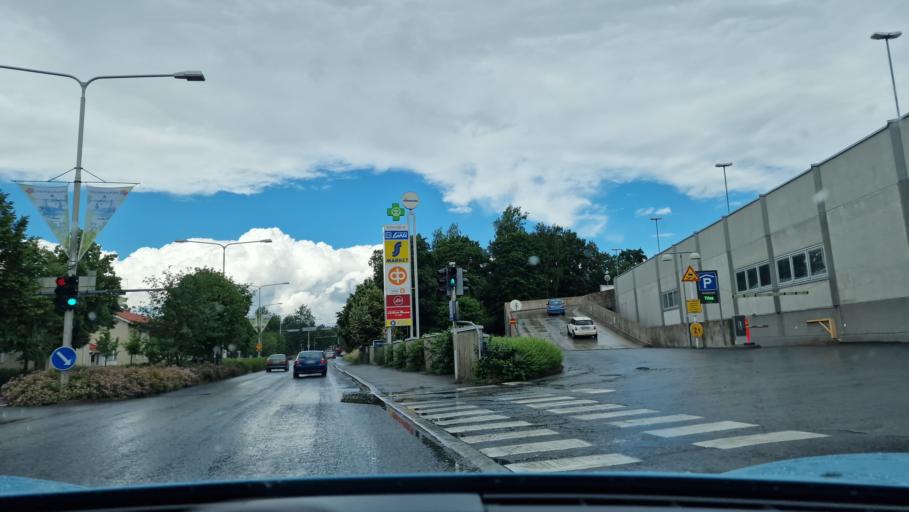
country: FI
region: Pirkanmaa
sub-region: Etelae-Pirkanmaa
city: Valkeakoski
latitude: 61.2662
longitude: 24.0277
